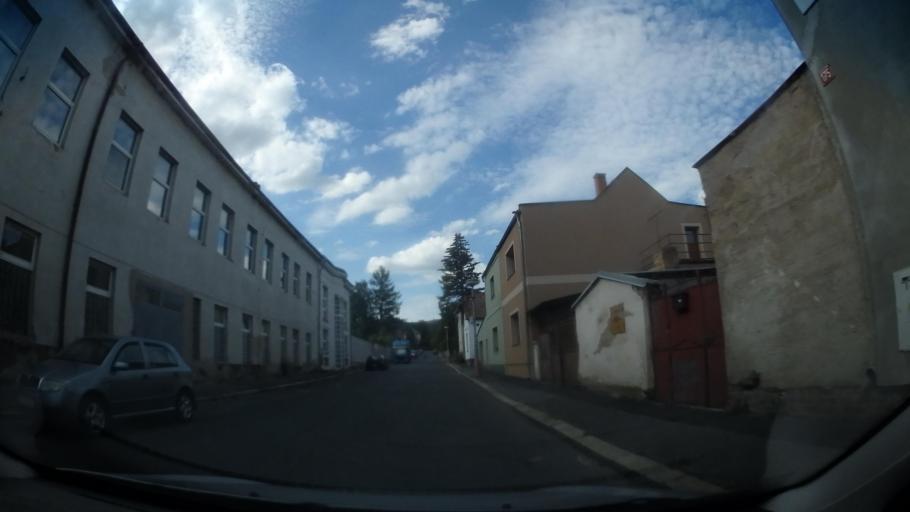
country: CZ
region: Central Bohemia
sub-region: Okres Kutna Hora
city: Kutna Hora
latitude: 49.9622
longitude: 15.2921
